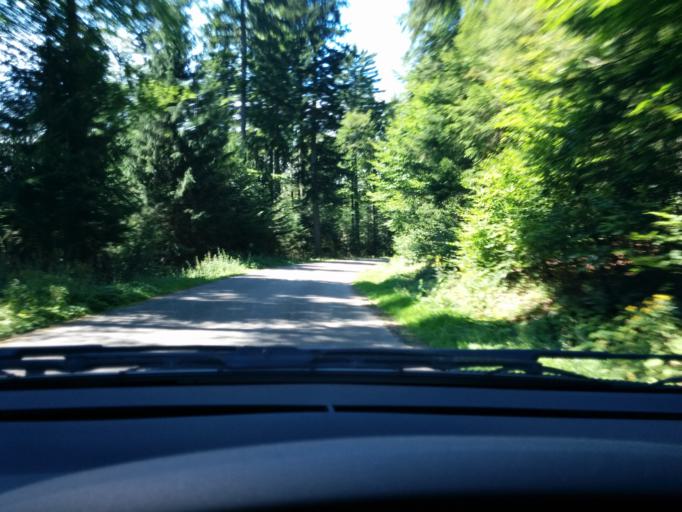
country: AT
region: Upper Austria
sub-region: Politischer Bezirk Rohrbach
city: Ulrichsberg
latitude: 48.6928
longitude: 13.9453
